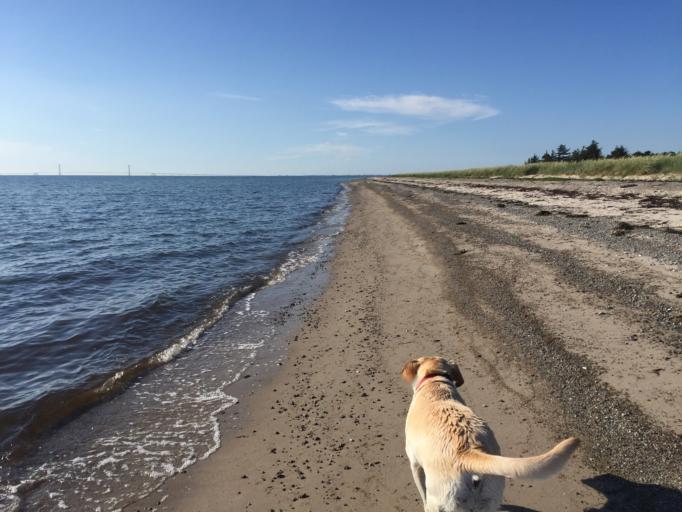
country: DK
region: Zealand
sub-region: Slagelse Kommune
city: Korsor
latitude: 55.2283
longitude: 11.1713
